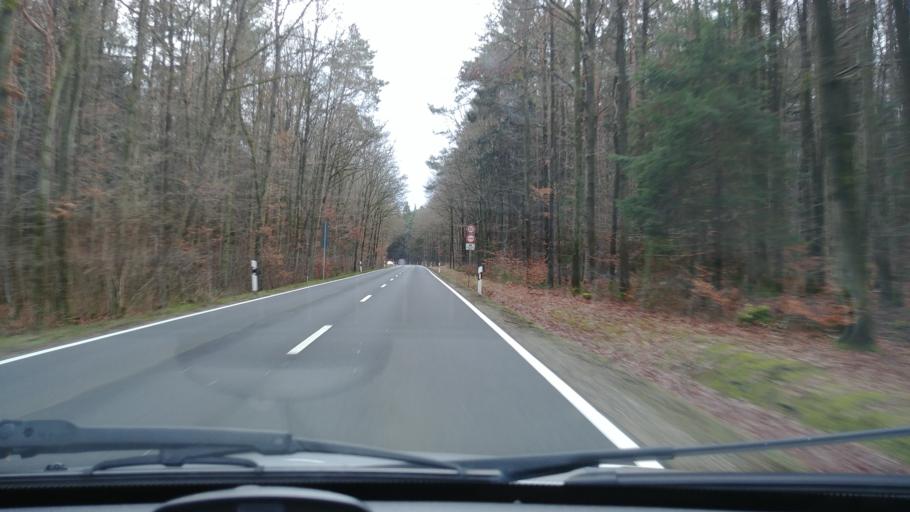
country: DE
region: Bavaria
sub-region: Regierungsbezirk Unterfranken
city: Erlenbach
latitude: 49.9994
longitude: 9.6309
